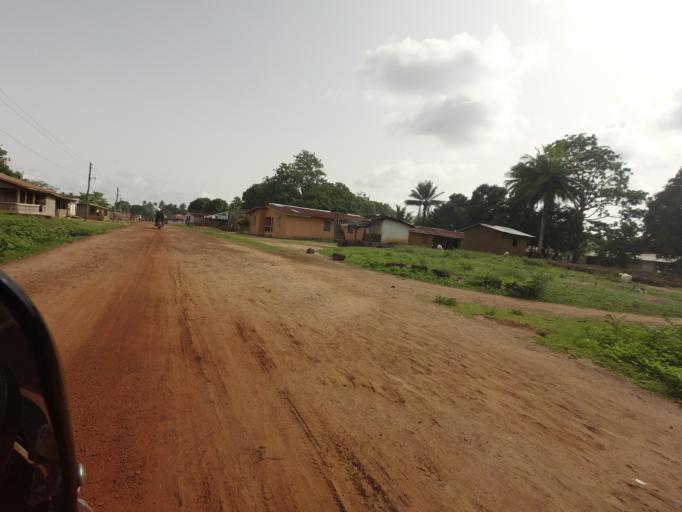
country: SL
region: Northern Province
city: Kassiri
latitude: 8.9401
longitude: -13.1150
